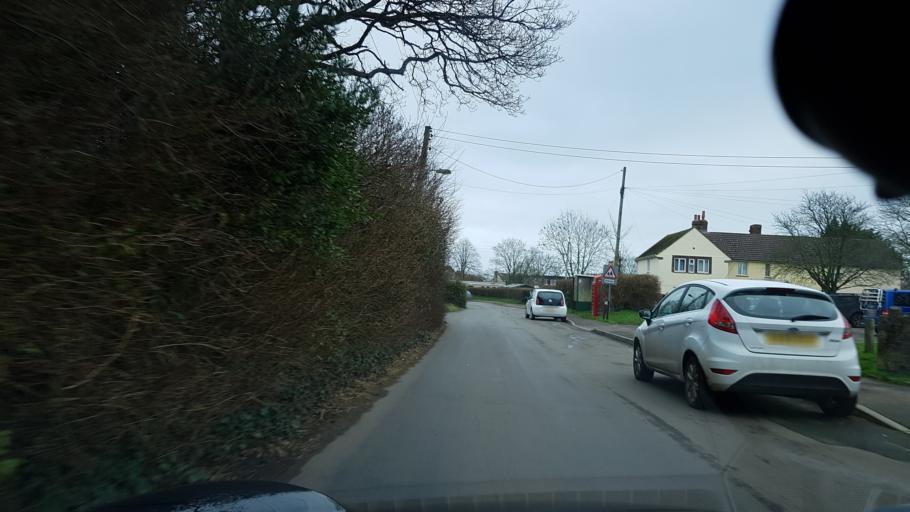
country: GB
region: England
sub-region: Somerset
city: Ilminster
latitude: 50.9351
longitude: -2.9635
